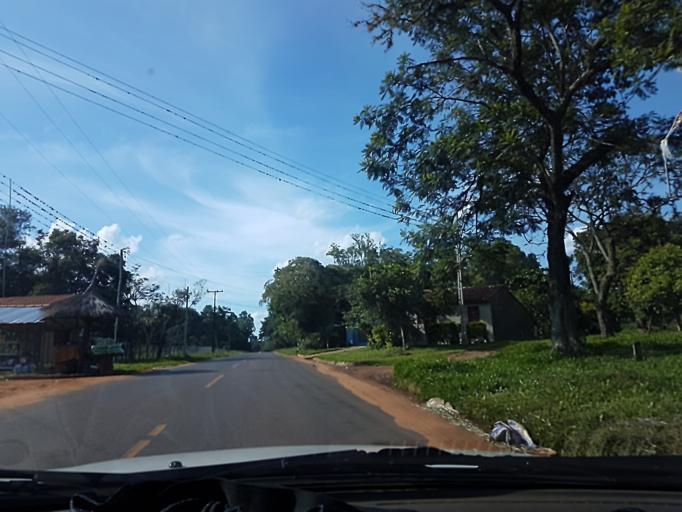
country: PY
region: Central
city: Limpio
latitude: -25.2024
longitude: -57.4520
